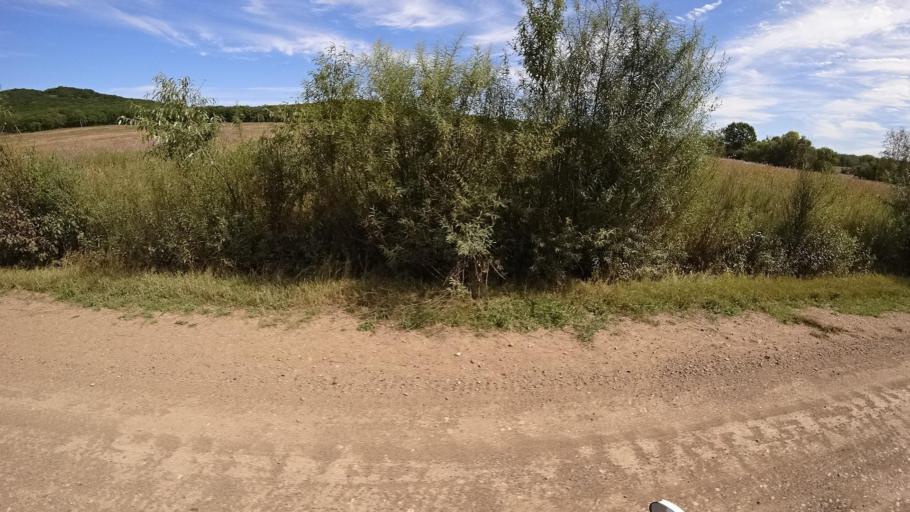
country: RU
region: Primorskiy
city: Yakovlevka
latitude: 44.7240
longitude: 133.6127
